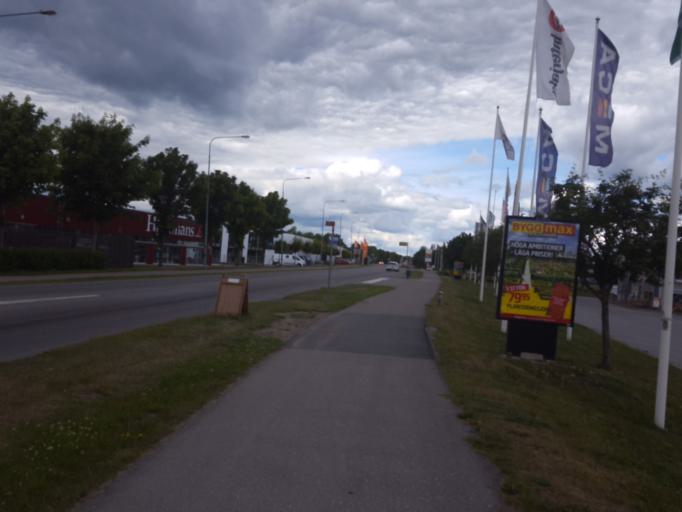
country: SE
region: Uppsala
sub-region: Uppsala Kommun
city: Saevja
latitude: 59.8563
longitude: 17.6907
